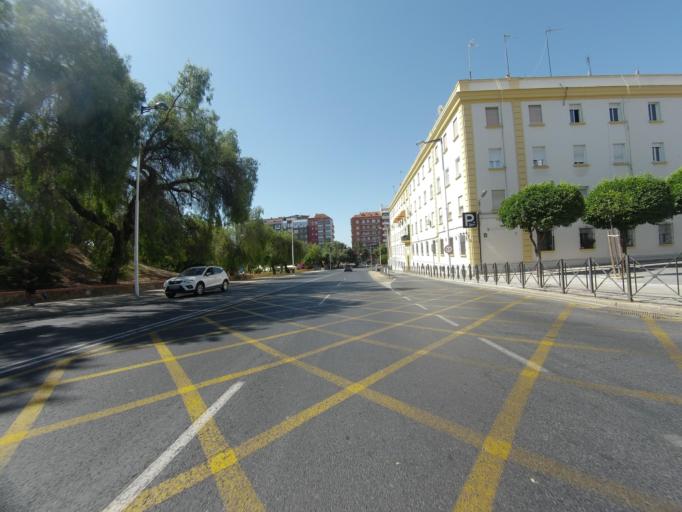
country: ES
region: Andalusia
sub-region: Provincia de Huelva
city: Huelva
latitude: 37.2556
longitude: -6.9413
